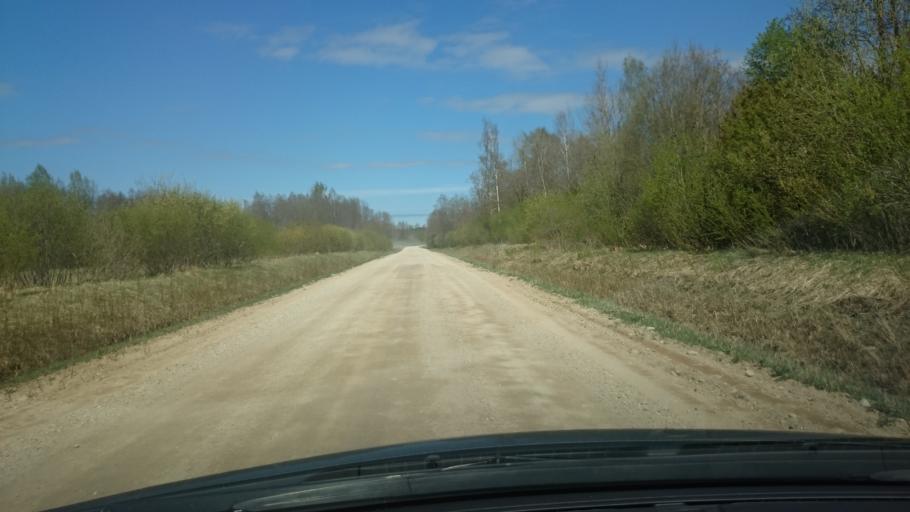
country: EE
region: Ida-Virumaa
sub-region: Sillamaee linn
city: Sillamae
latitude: 59.1079
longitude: 27.7965
